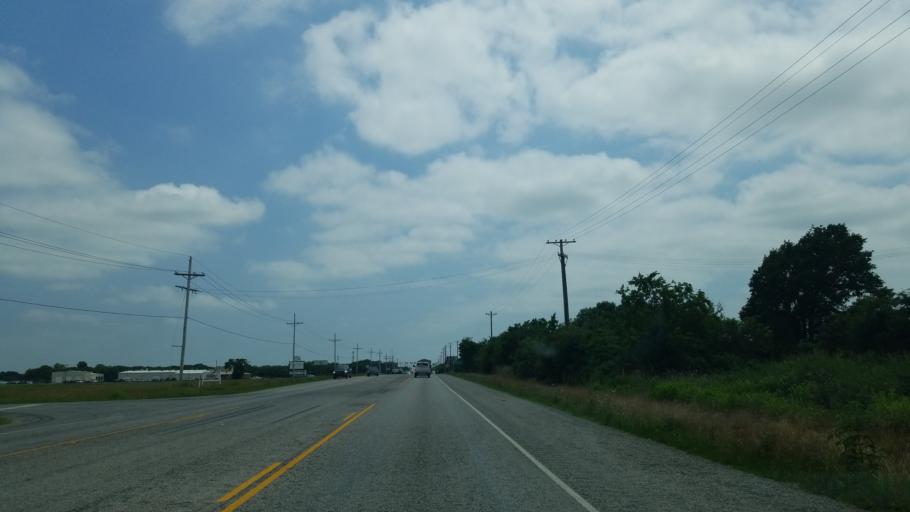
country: US
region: Texas
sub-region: Denton County
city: Pilot Point
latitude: 33.3735
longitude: -96.9633
